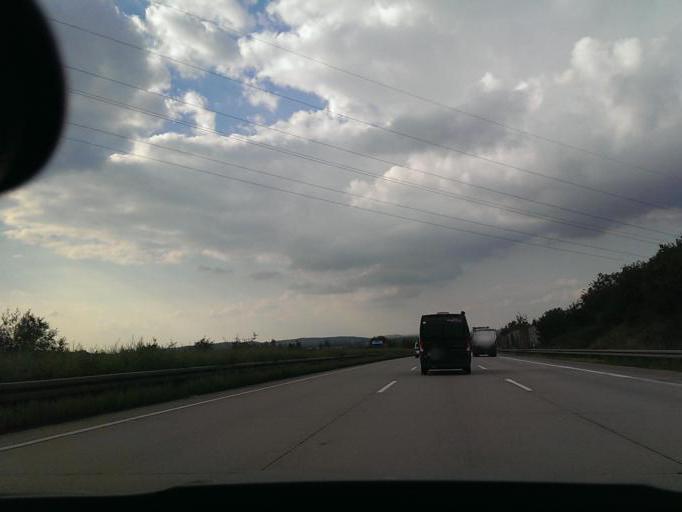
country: DE
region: Lower Saxony
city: Hildesheim
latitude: 52.1409
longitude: 10.0030
